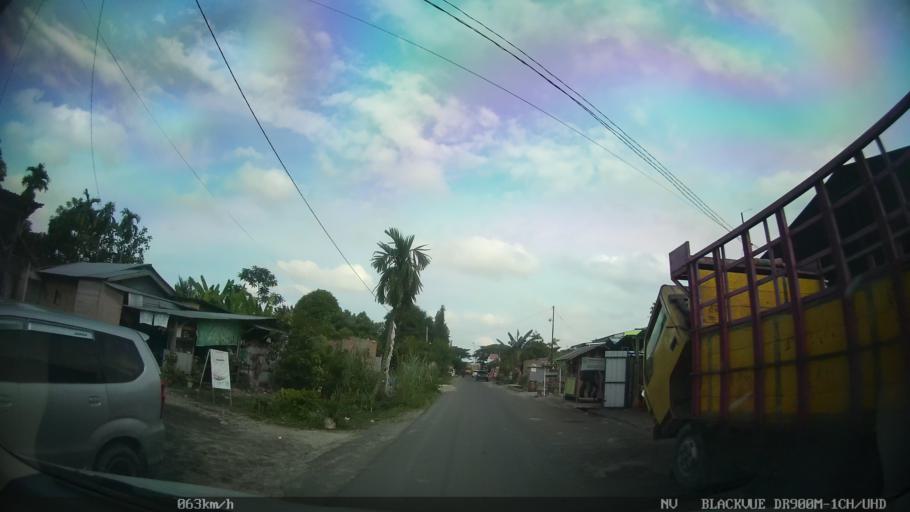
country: ID
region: North Sumatra
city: Percut
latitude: 3.5650
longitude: 98.7915
